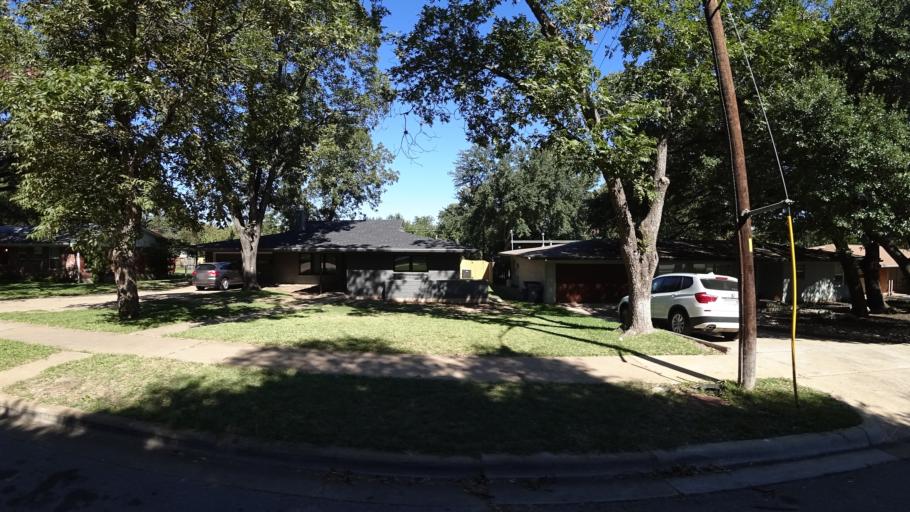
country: US
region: Texas
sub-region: Travis County
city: West Lake Hills
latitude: 30.3370
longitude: -97.7518
